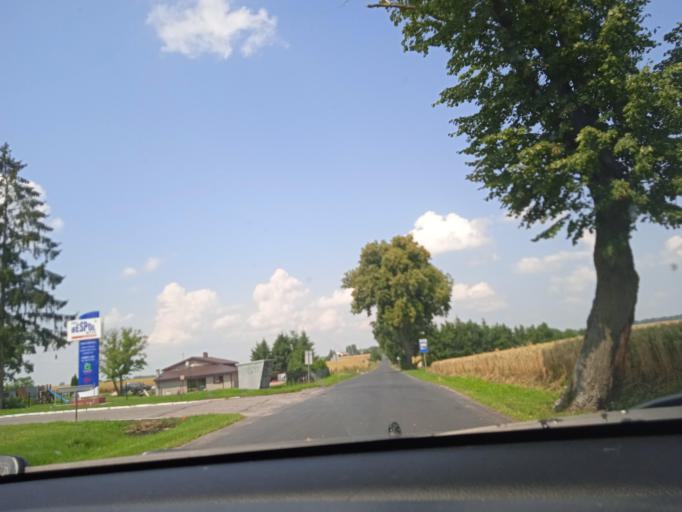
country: PL
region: Kujawsko-Pomorskie
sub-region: Powiat grudziadzki
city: Lasin
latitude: 53.5388
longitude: 19.0685
